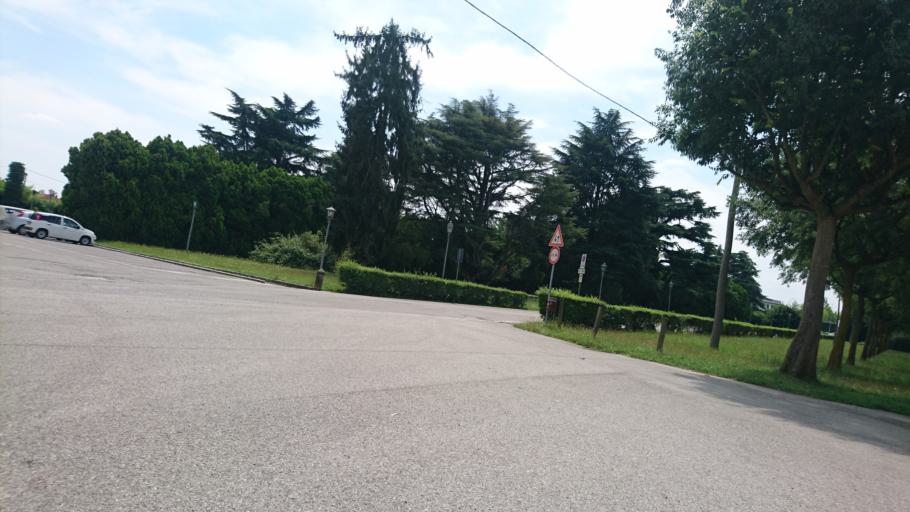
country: IT
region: Veneto
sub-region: Provincia di Padova
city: Caselle
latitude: 45.4127
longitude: 11.8484
